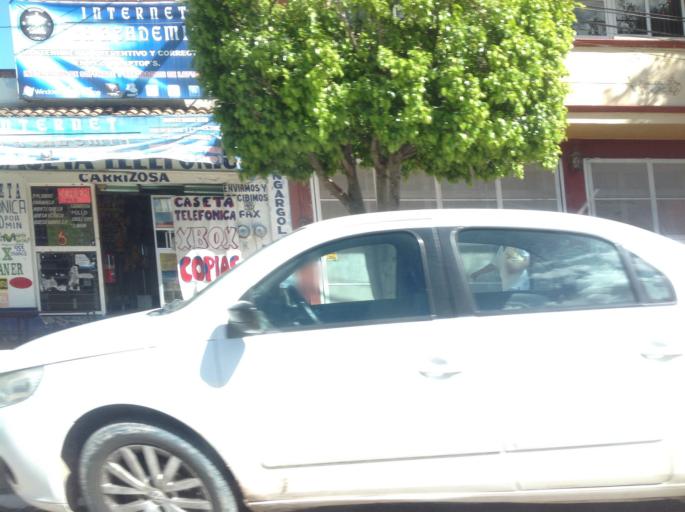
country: MX
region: Oaxaca
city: Ciudad de Huajuapam de Leon
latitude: 17.8115
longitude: -97.7709
